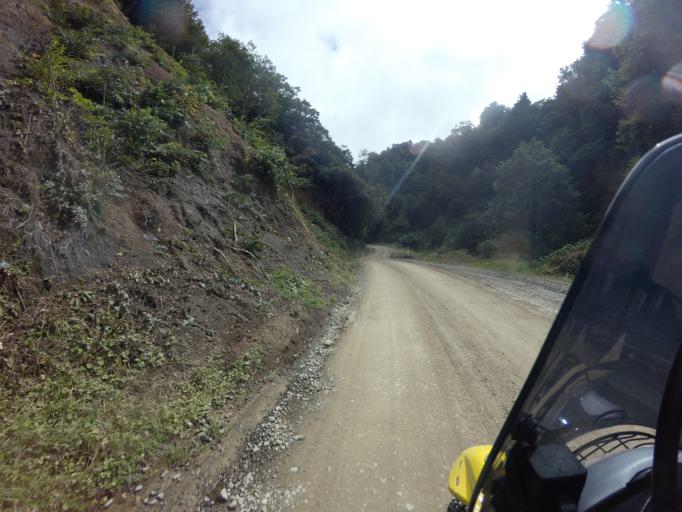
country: NZ
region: Bay of Plenty
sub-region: Whakatane District
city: Murupara
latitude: -38.6489
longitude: 177.0344
